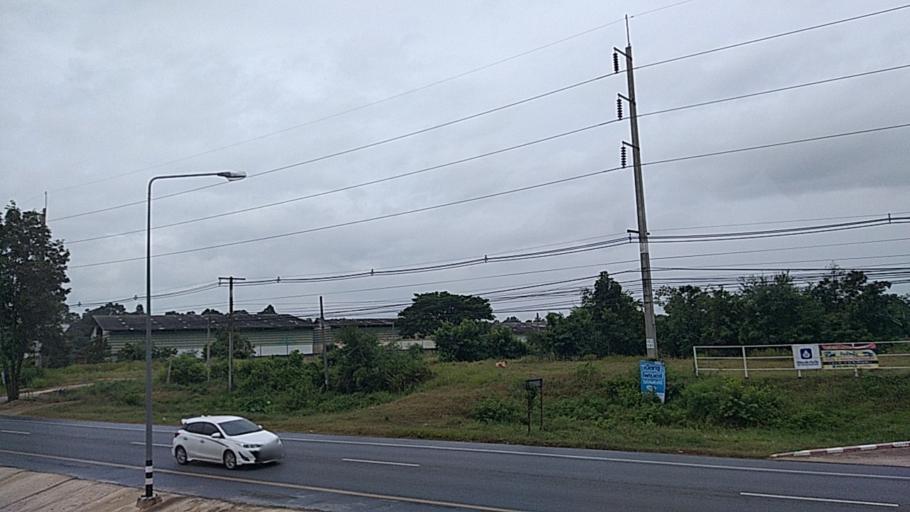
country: TH
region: Maha Sarakham
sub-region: Amphoe Borabue
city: Borabue
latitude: 16.0497
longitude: 103.1280
